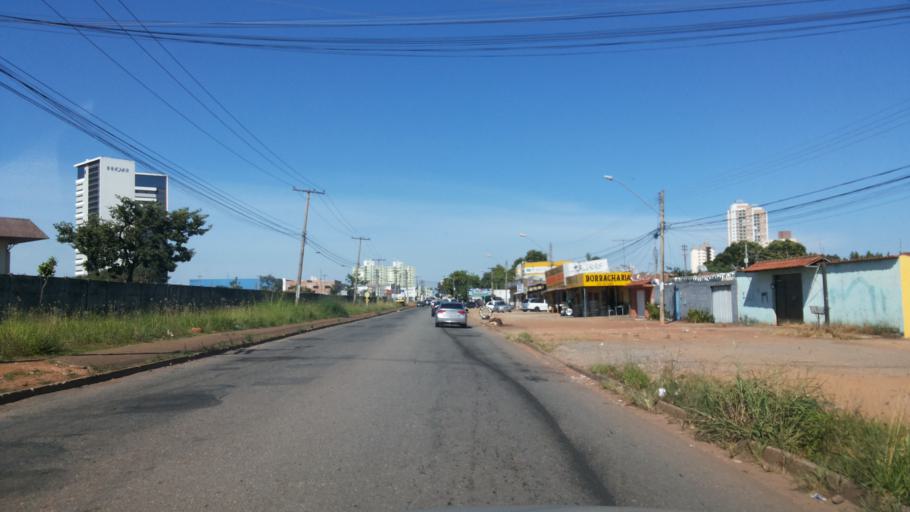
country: BR
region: Goias
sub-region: Goiania
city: Goiania
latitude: -16.7307
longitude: -49.2639
